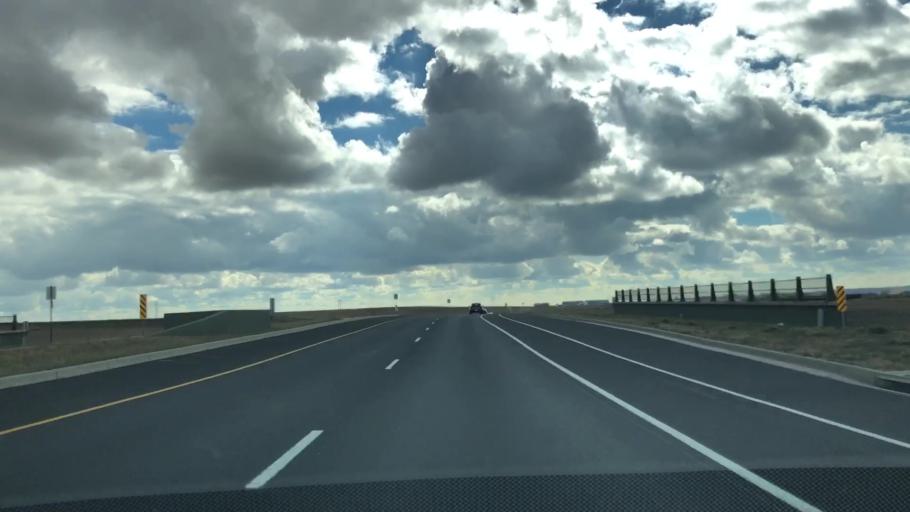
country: US
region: Colorado
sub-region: Larimer County
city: Loveland
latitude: 40.4216
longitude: -104.9845
